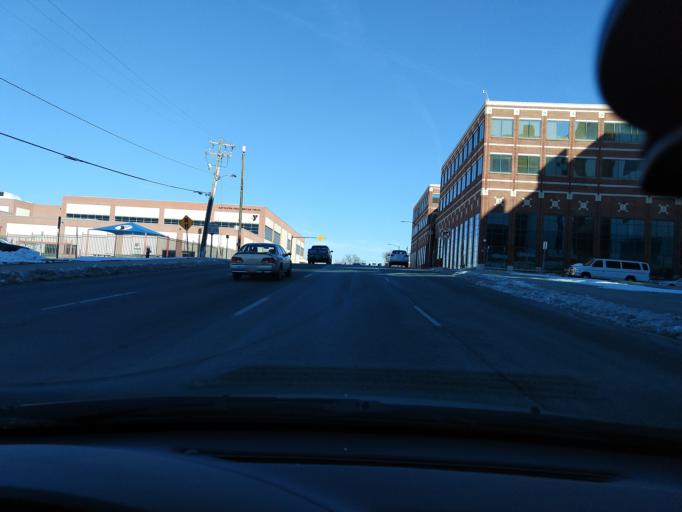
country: US
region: North Carolina
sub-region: Guilford County
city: Greensboro
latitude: 36.0715
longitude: -79.7962
